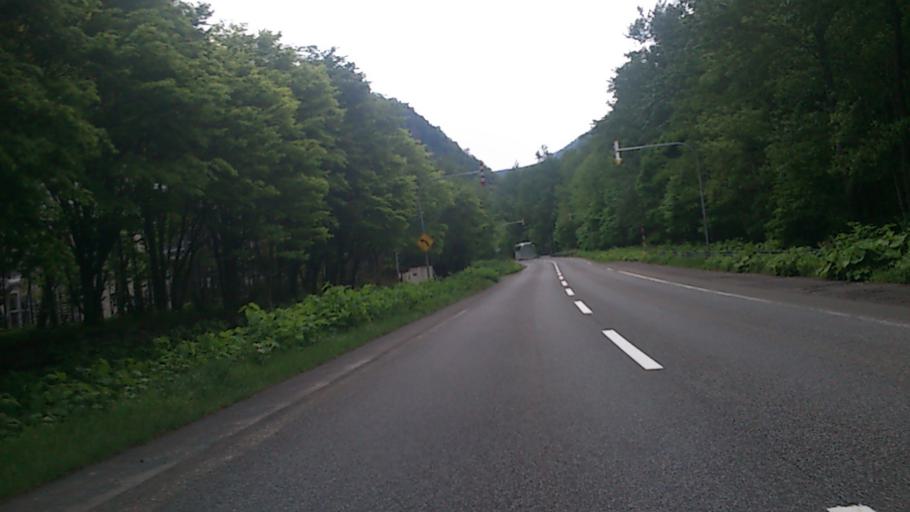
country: JP
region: Hokkaido
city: Kamikawa
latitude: 43.7521
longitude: 142.9311
